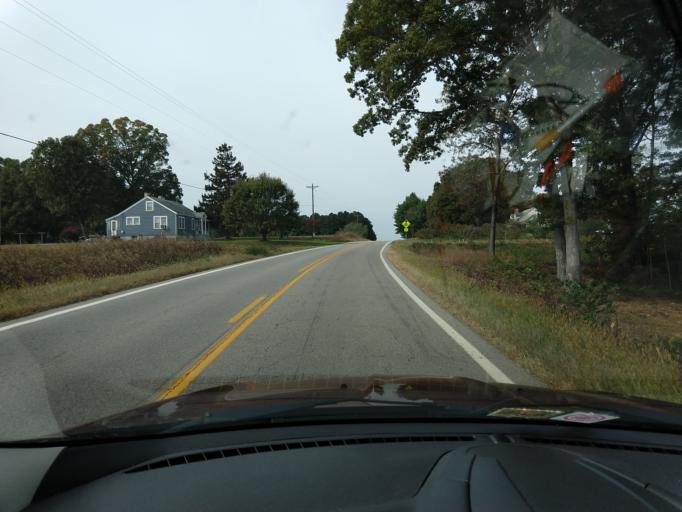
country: US
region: Virginia
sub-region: Pittsylvania County
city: Gretna
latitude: 36.9451
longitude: -79.4647
